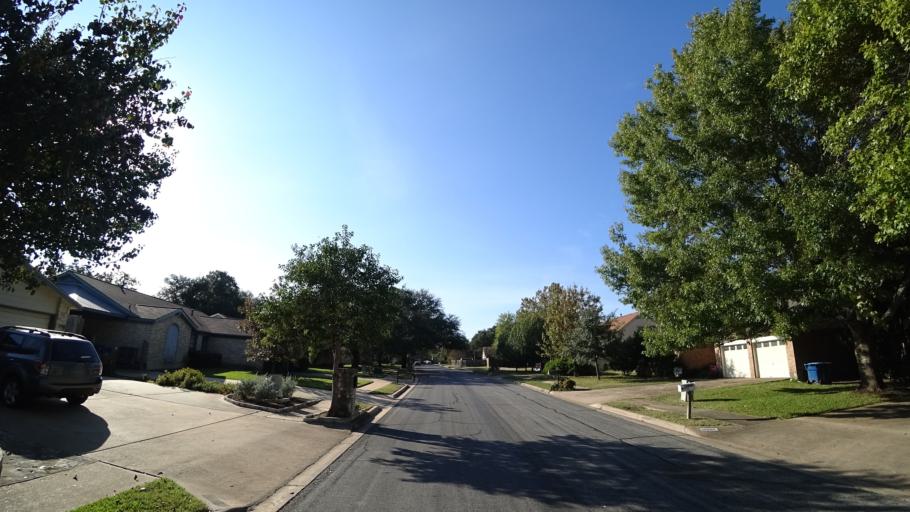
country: US
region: Texas
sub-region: Williamson County
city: Anderson Mill
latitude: 30.4496
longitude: -97.8117
